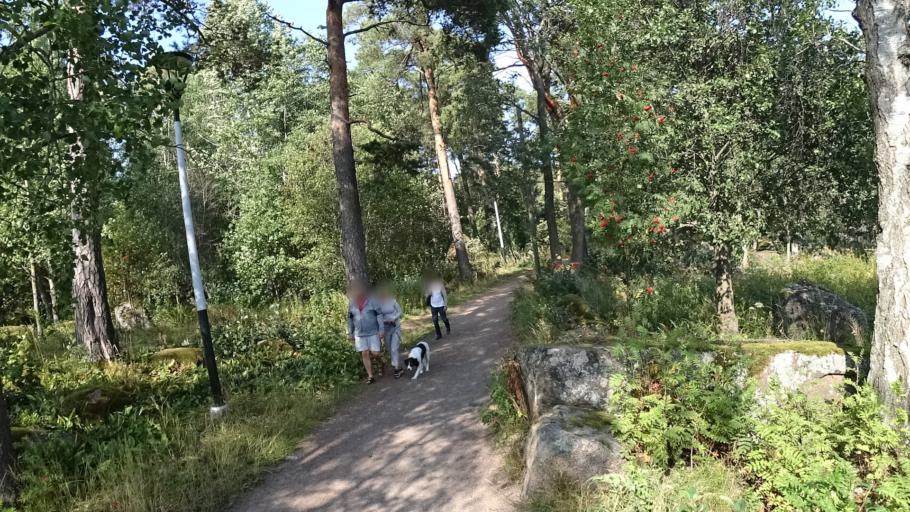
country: FI
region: Kymenlaakso
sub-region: Kotka-Hamina
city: Kotka
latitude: 60.4476
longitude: 26.9429
